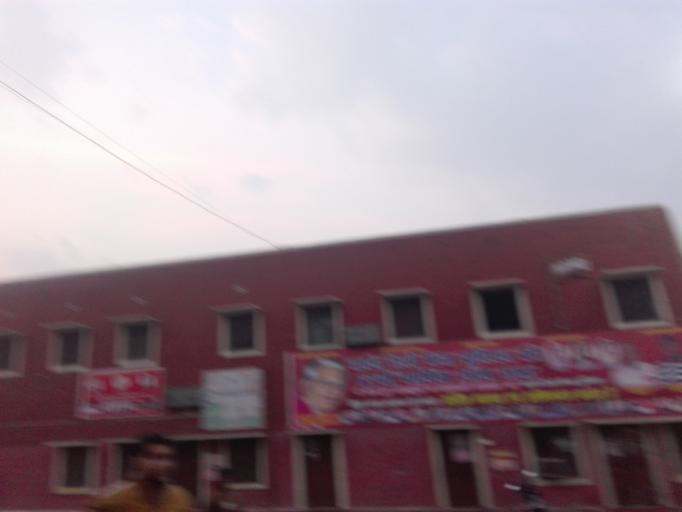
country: IN
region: Uttar Pradesh
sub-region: Lucknow District
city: Lucknow
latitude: 26.8316
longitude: 80.9262
